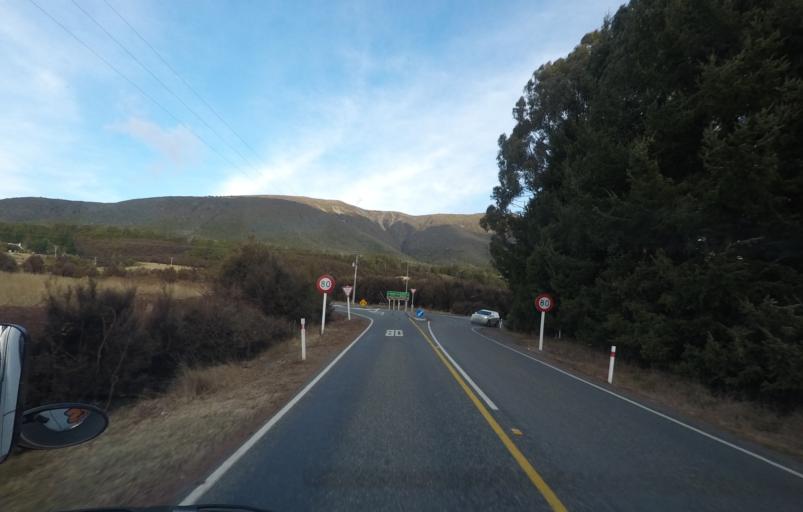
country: NZ
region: Tasman
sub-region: Tasman District
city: Wakefield
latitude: -41.7847
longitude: 172.8935
